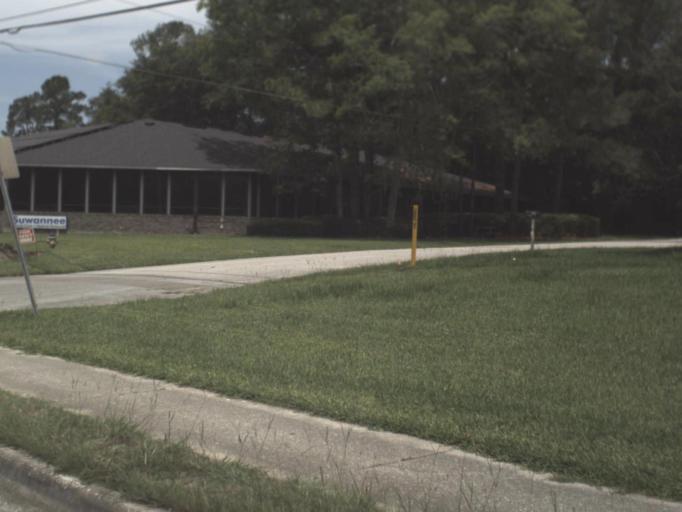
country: US
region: Florida
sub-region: Alachua County
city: Gainesville
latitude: 29.6596
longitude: -82.4021
